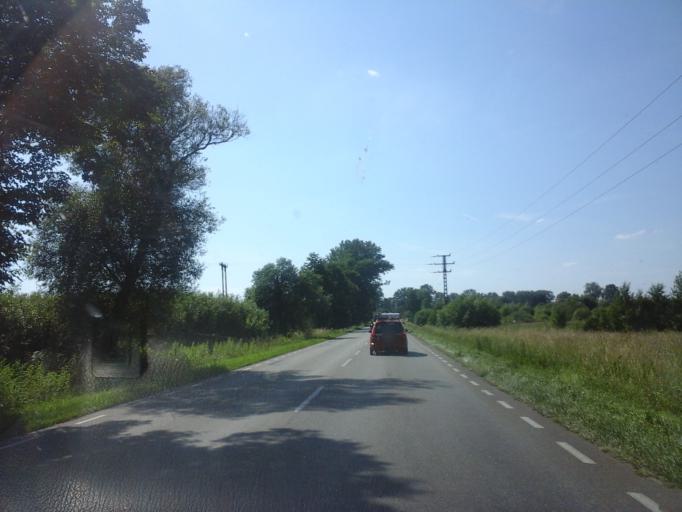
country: PL
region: West Pomeranian Voivodeship
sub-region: Powiat bialogardzki
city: Karlino
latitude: 54.0287
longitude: 15.9083
